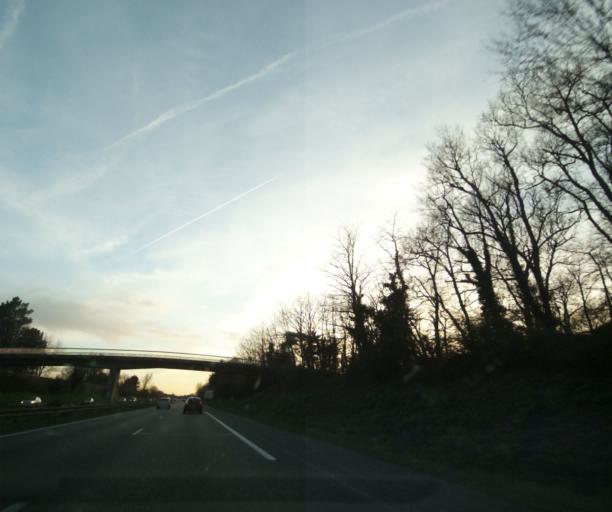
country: FR
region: Aquitaine
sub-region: Departement de la Gironde
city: Eysines
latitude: 44.8721
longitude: -0.6410
